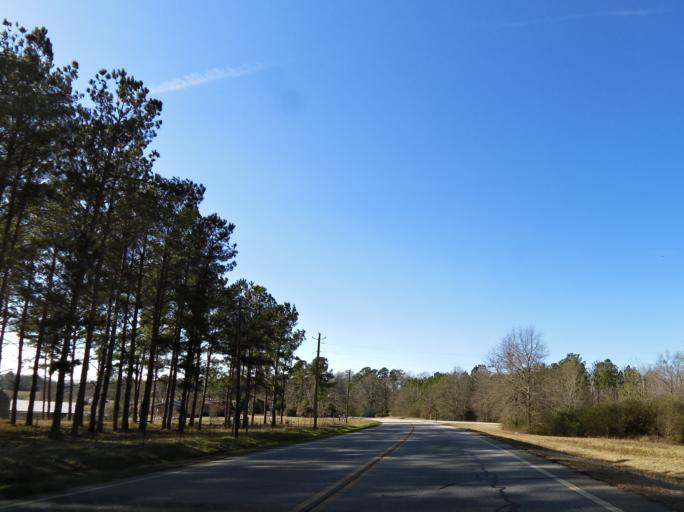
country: US
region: Georgia
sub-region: Lamar County
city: Barnesville
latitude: 32.9164
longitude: -84.1301
